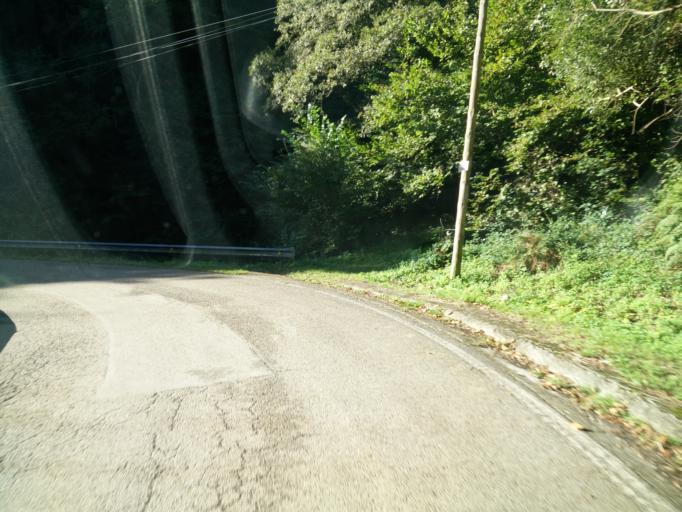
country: ES
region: Cantabria
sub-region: Provincia de Cantabria
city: San Pedro del Romeral
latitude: 43.1237
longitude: -3.8133
